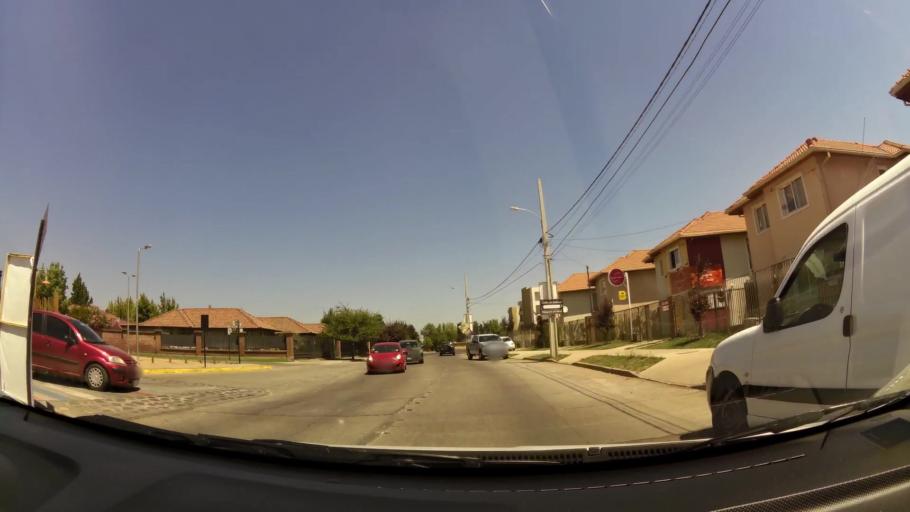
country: CL
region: Maule
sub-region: Provincia de Talca
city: Talca
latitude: -35.4315
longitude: -71.6223
